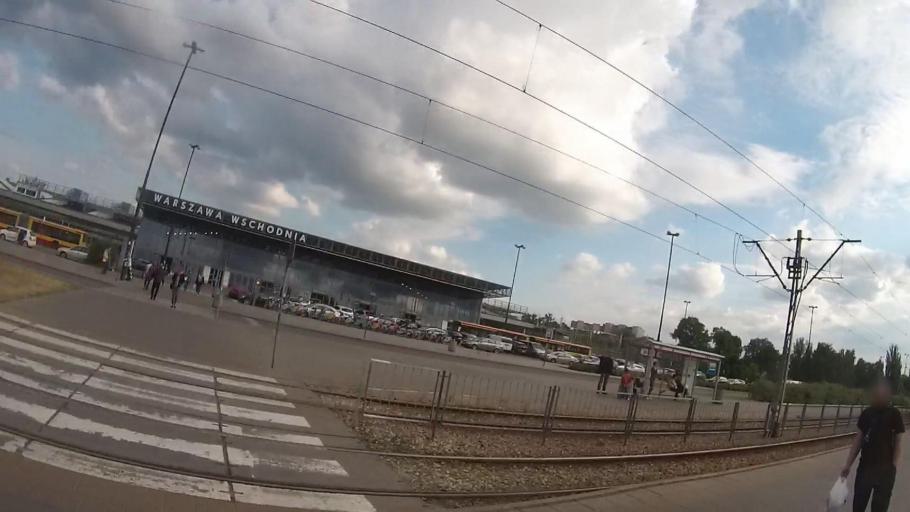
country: PL
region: Masovian Voivodeship
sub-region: Warszawa
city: Praga Polnoc
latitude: 52.2530
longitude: 21.0505
